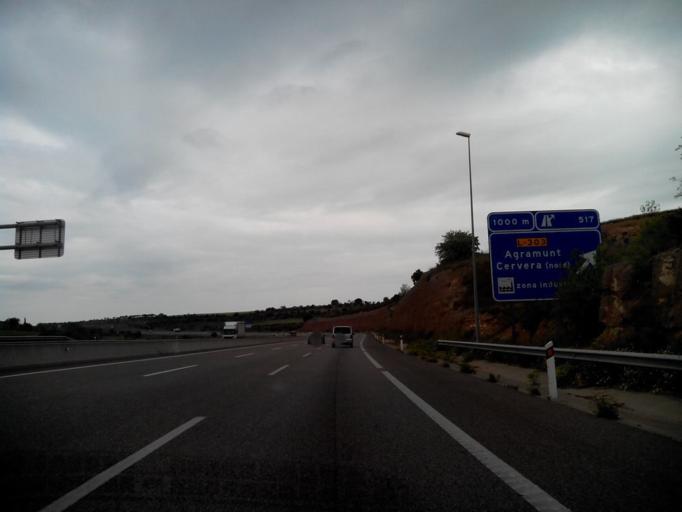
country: ES
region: Catalonia
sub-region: Provincia de Lleida
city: Cervera
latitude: 41.6863
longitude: 1.2683
